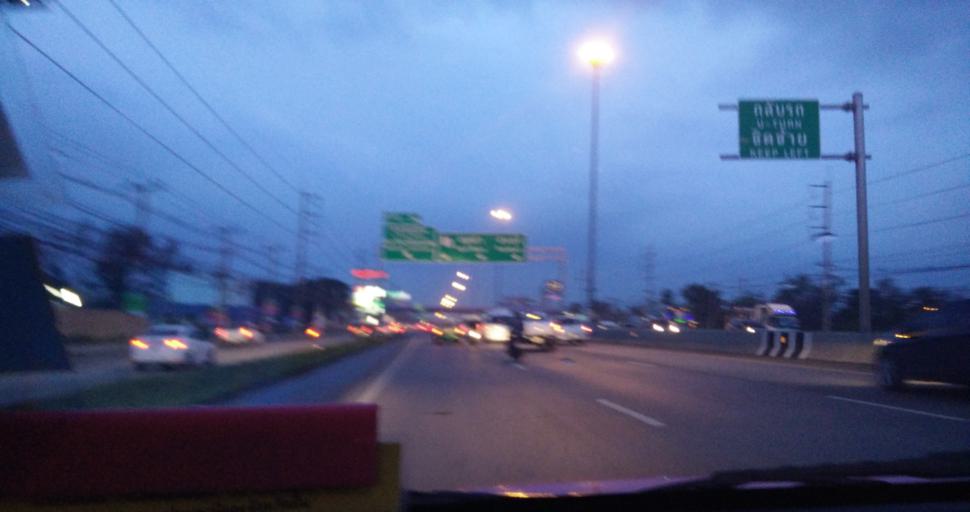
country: TH
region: Pathum Thani
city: Khlong Luang
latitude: 14.0232
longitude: 100.6156
